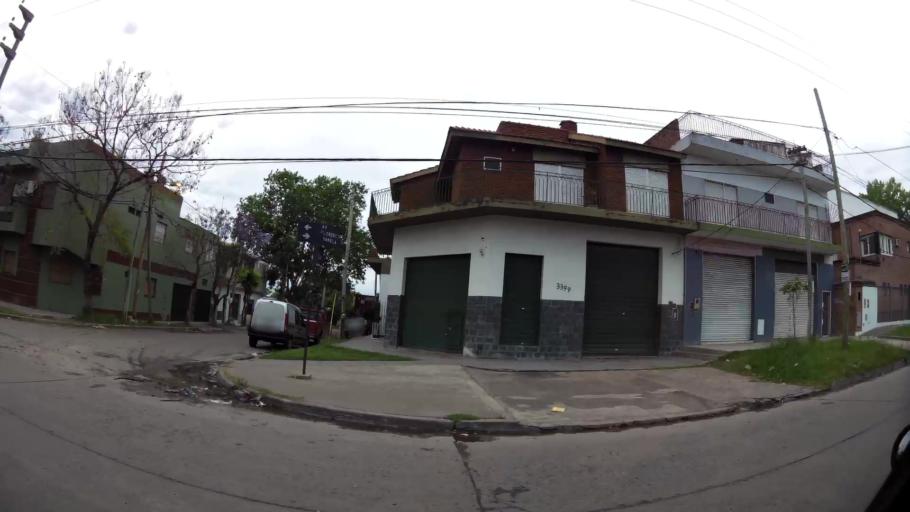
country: AR
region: Buenos Aires
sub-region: Partido de Quilmes
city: Quilmes
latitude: -34.7561
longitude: -58.2344
